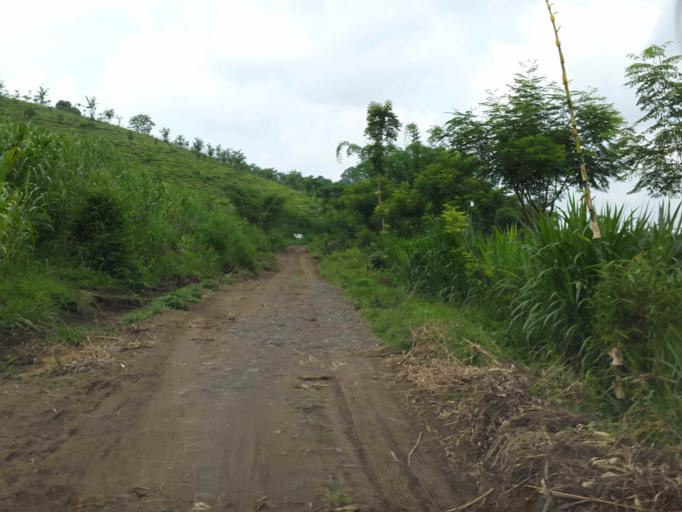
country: ID
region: East Java
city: Pandansari
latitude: -8.0889
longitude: 112.7943
